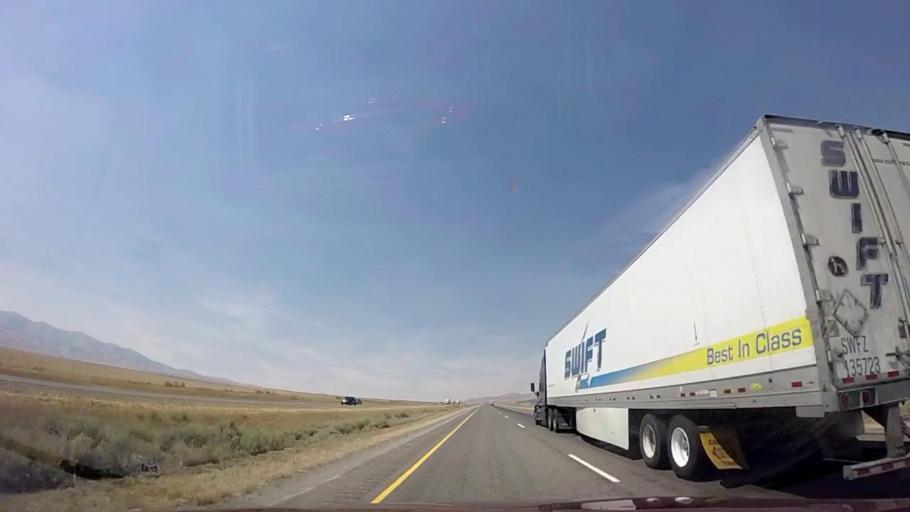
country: US
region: Idaho
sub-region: Power County
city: American Falls
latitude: 42.1355
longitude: -112.9732
